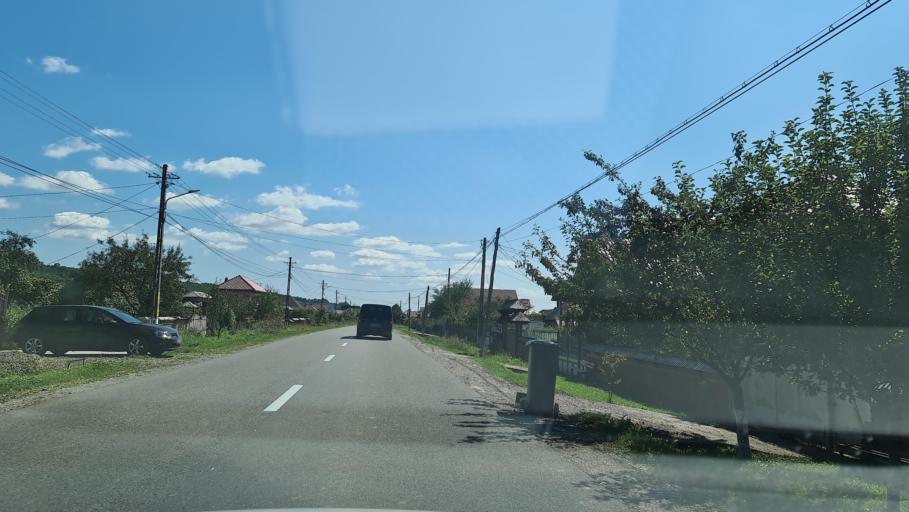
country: RO
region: Bacau
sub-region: Comuna Balcani
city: Ludasi
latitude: 46.6411
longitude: 26.5718
